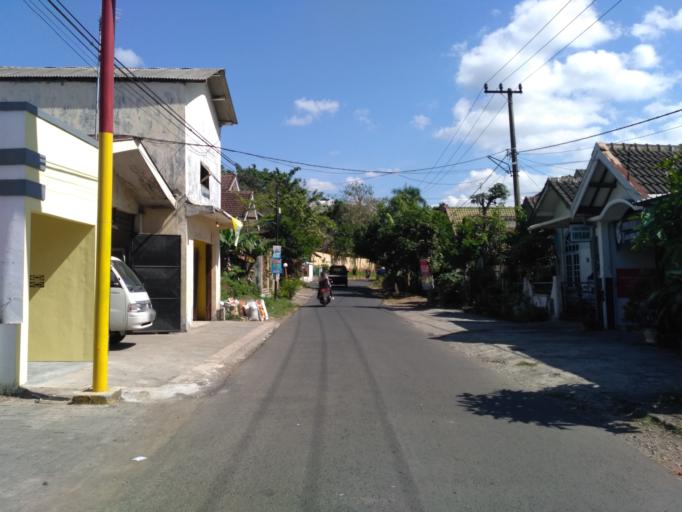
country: ID
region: East Java
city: Singosari
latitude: -7.9041
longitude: 112.6636
